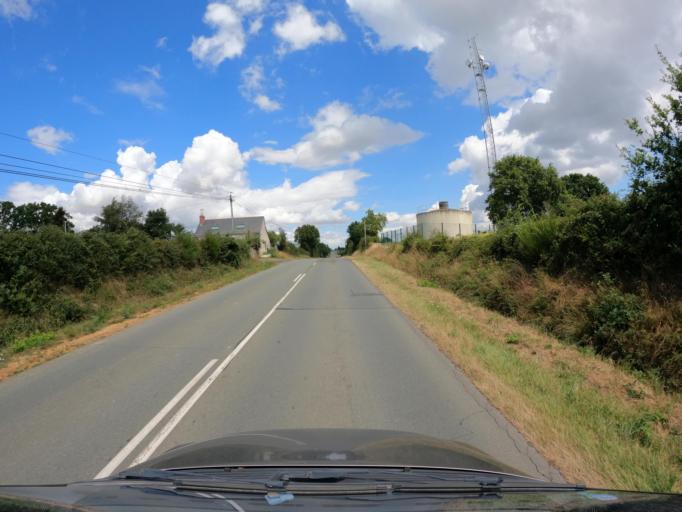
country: FR
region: Pays de la Loire
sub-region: Departement de Maine-et-Loire
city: Champigne
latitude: 47.6723
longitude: -0.5663
